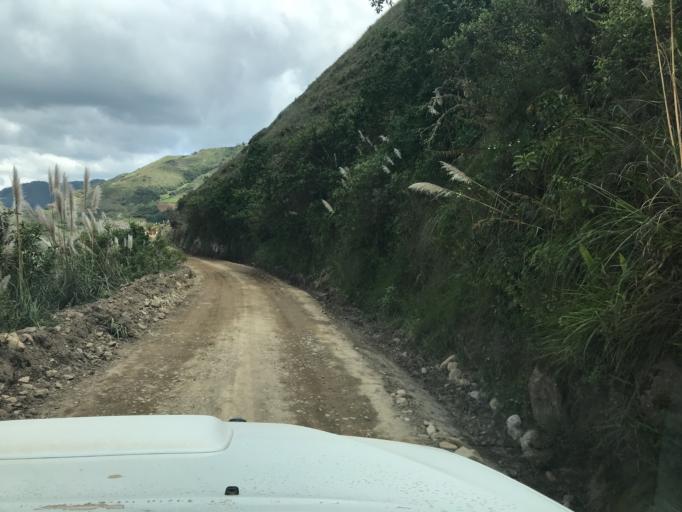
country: PE
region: Cajamarca
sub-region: Provincia de Chota
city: Querocoto
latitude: -6.3683
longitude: -79.0368
